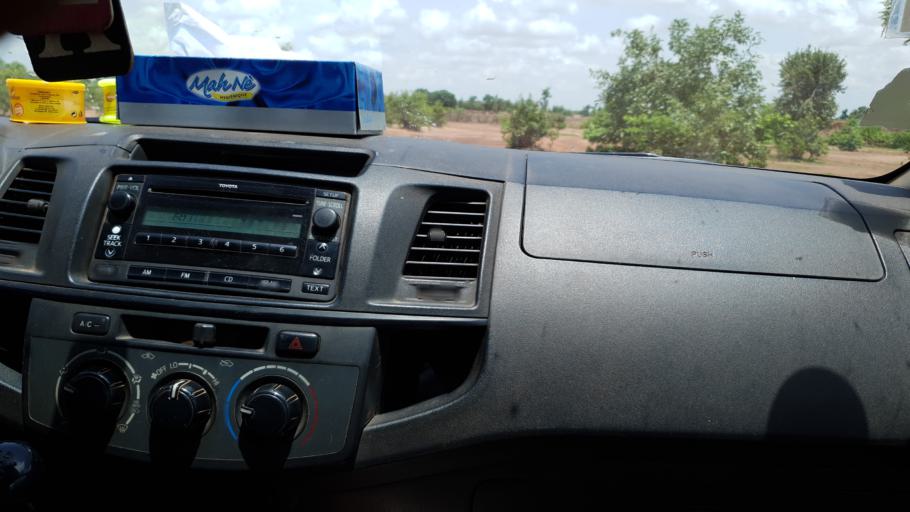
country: ML
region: Koulikoro
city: Banamba
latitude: 13.3772
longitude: -7.2167
